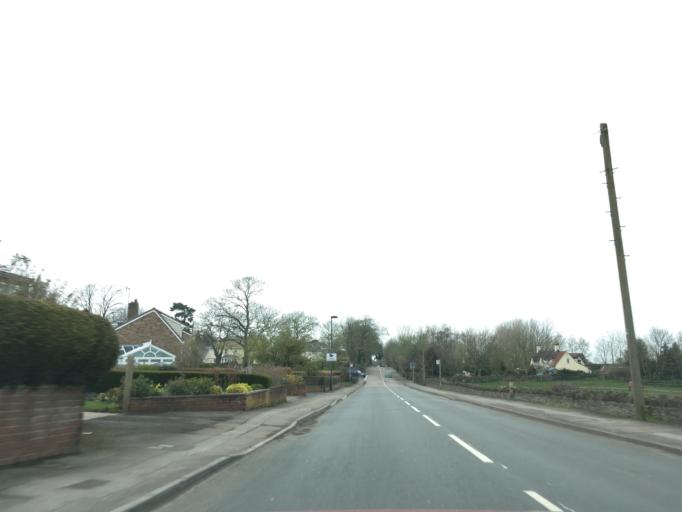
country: GB
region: England
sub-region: South Gloucestershire
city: Winterbourne
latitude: 51.5201
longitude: -2.4999
